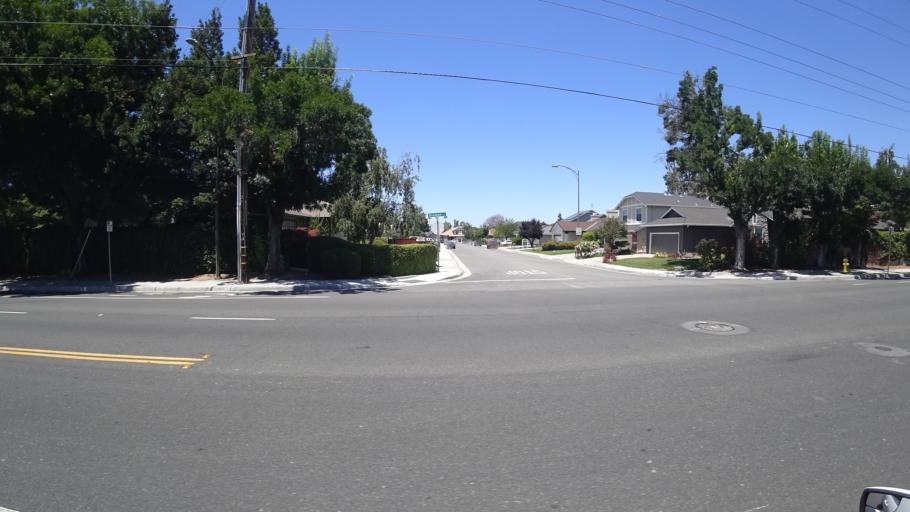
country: US
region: California
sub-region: Santa Clara County
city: Seven Trees
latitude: 37.2618
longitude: -121.8811
